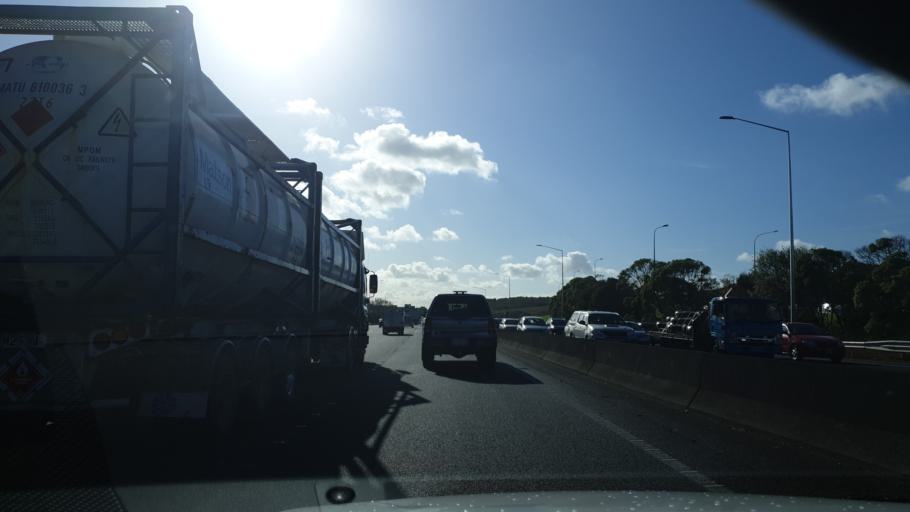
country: NZ
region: Auckland
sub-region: Auckland
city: Tamaki
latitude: -36.9153
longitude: 174.8270
